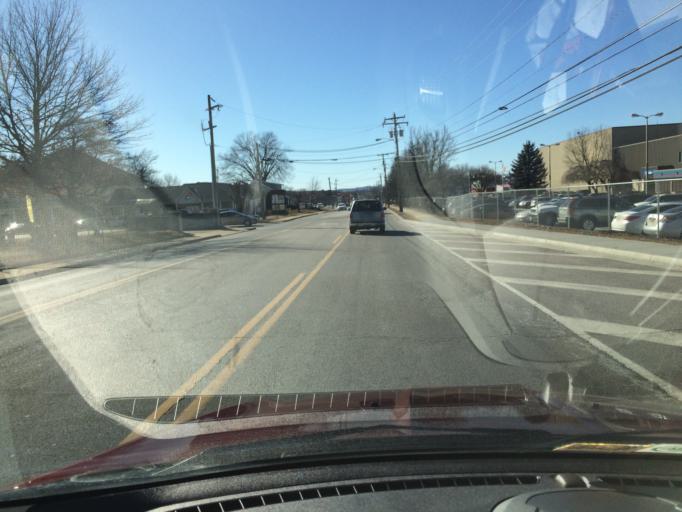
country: US
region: Virginia
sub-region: Rockingham County
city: Bridgewater
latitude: 38.3919
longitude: -78.9646
